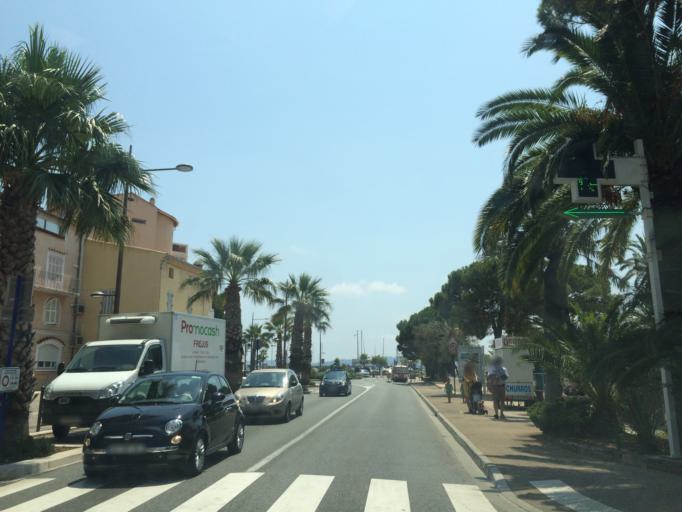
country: FR
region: Provence-Alpes-Cote d'Azur
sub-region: Departement du Var
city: Sainte-Maxime
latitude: 43.3077
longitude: 6.6401
